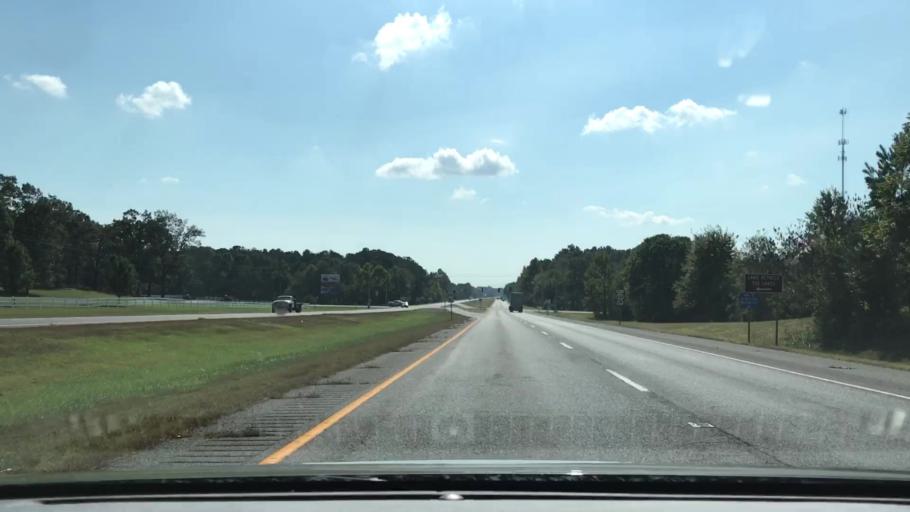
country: US
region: Kentucky
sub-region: Marshall County
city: Benton
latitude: 36.7671
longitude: -88.3125
